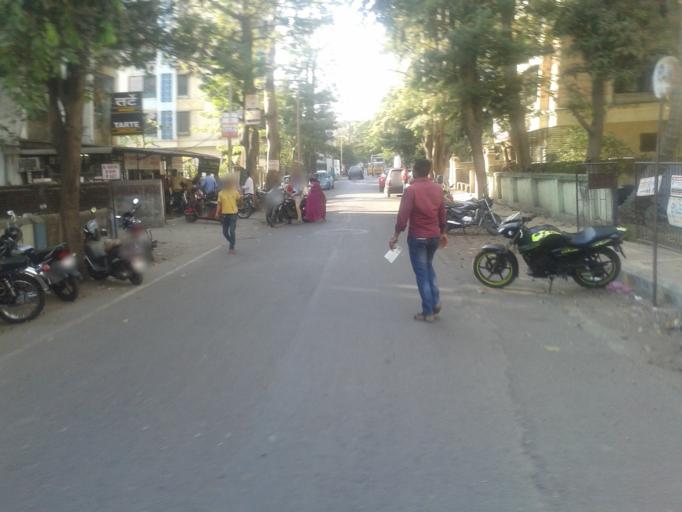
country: IN
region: Maharashtra
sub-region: Thane
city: Dombivli
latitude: 19.2051
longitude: 73.0910
